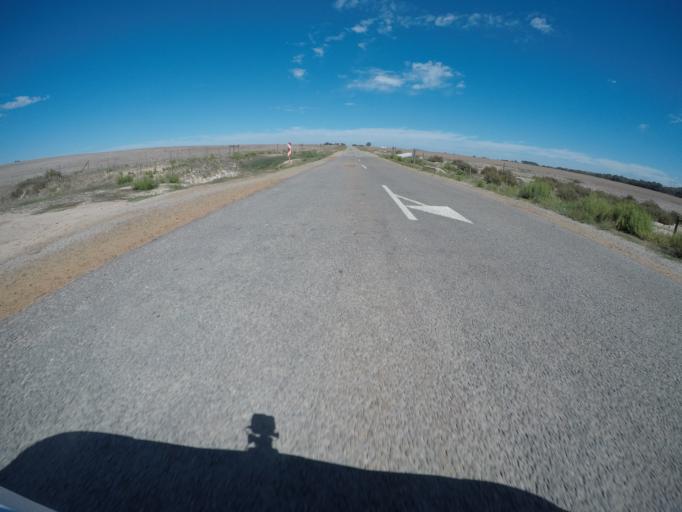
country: ZA
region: Western Cape
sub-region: City of Cape Town
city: Atlantis
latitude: -33.6031
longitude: 18.6405
